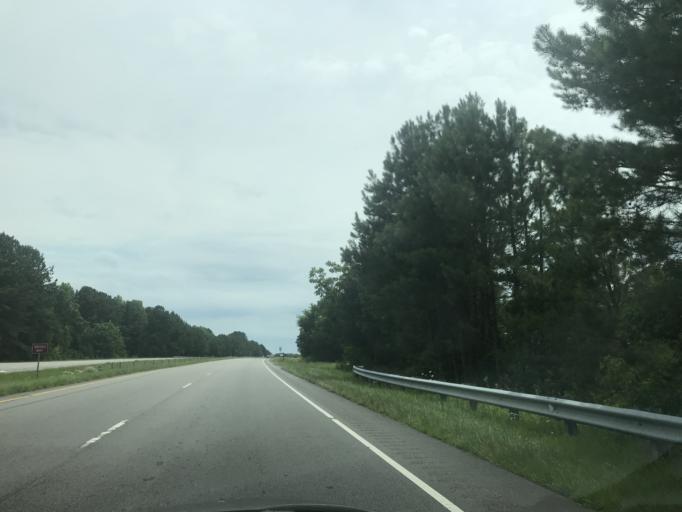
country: US
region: North Carolina
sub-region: Vance County
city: South Henderson
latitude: 36.2398
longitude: -78.4365
